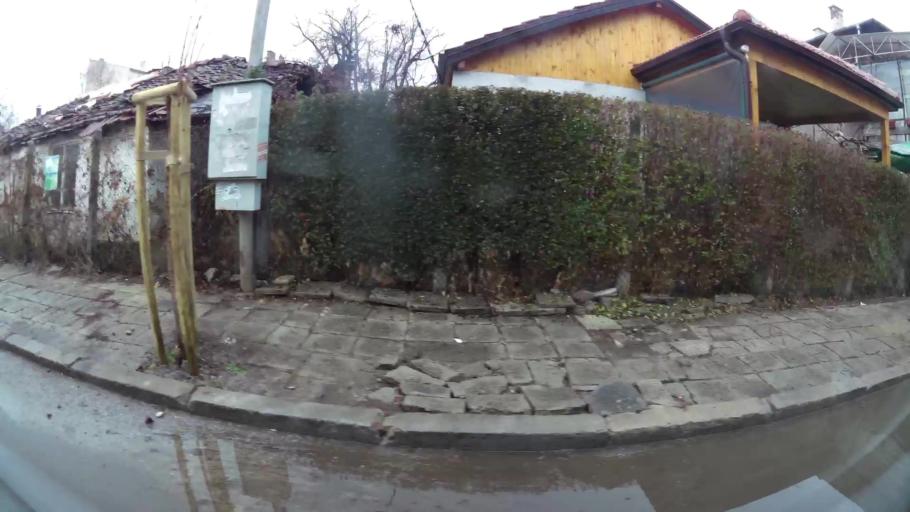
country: BG
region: Sofia-Capital
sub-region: Stolichna Obshtina
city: Sofia
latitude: 42.7298
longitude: 23.3008
